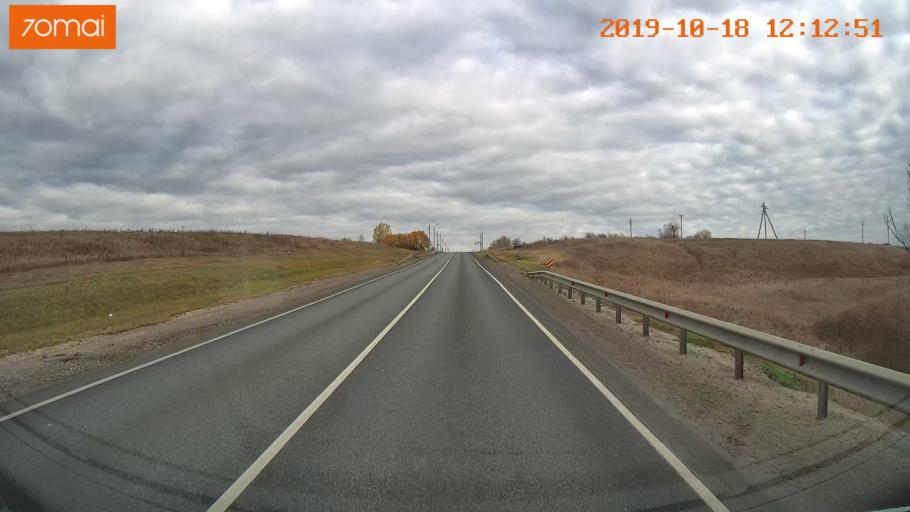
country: RU
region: Rjazan
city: Zakharovo
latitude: 54.4160
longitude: 39.3634
